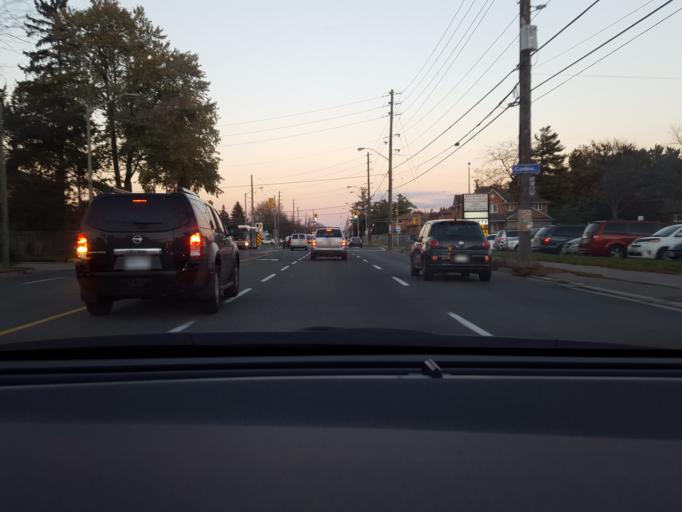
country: CA
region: Ontario
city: Scarborough
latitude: 43.7876
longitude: -79.1844
